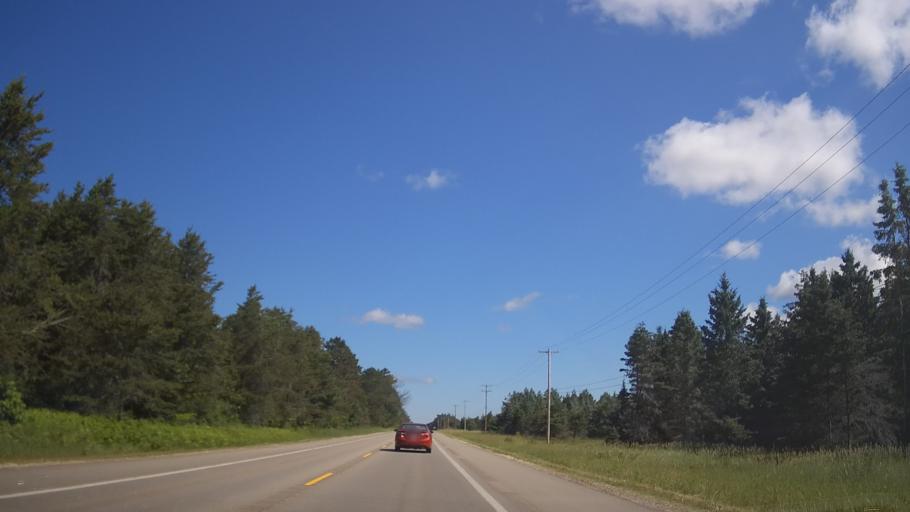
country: US
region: Michigan
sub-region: Cheboygan County
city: Indian River
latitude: 45.4794
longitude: -84.7811
